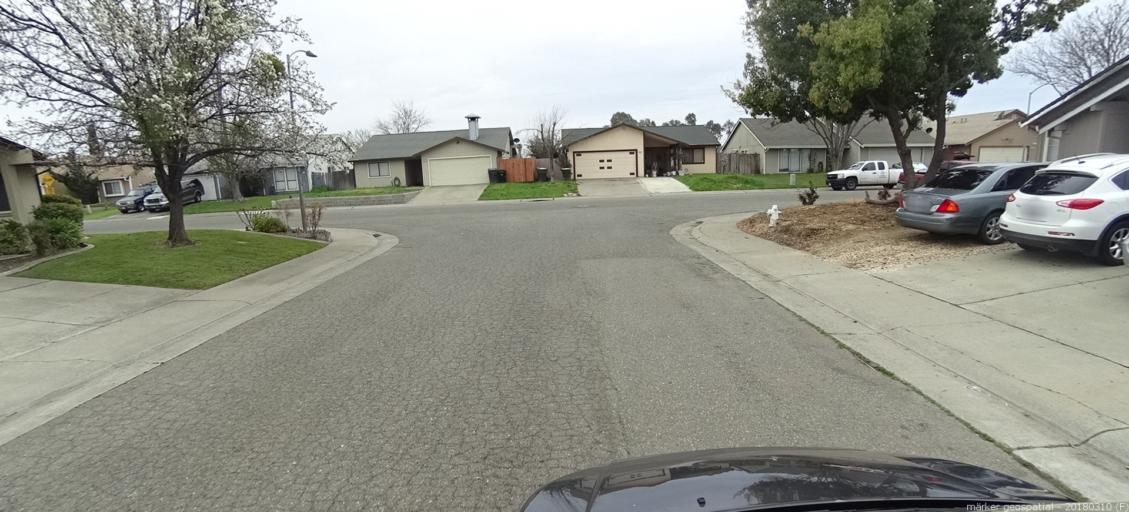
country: US
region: California
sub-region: Sacramento County
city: Florin
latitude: 38.4750
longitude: -121.3839
